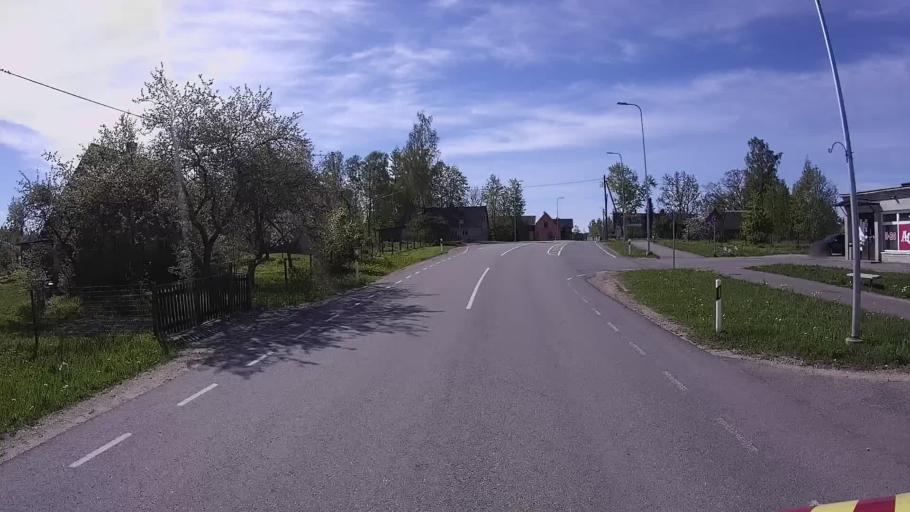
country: EE
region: Polvamaa
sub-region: Raepina vald
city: Rapina
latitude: 58.0059
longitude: 27.5426
